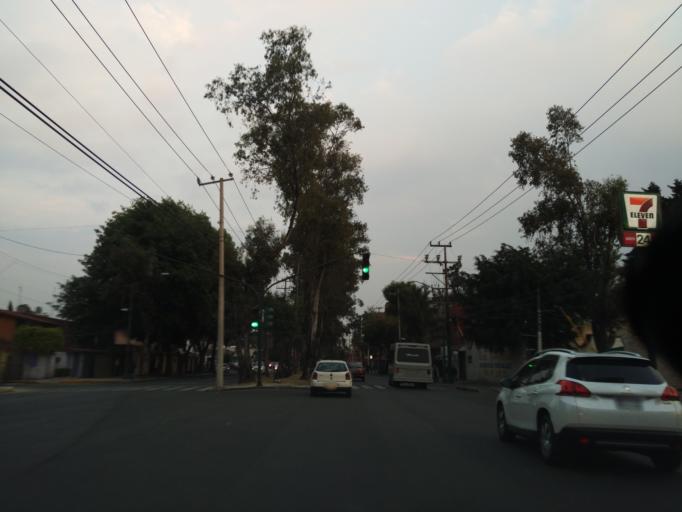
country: MX
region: Mexico City
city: Xochimilco
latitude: 19.3016
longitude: -99.1179
